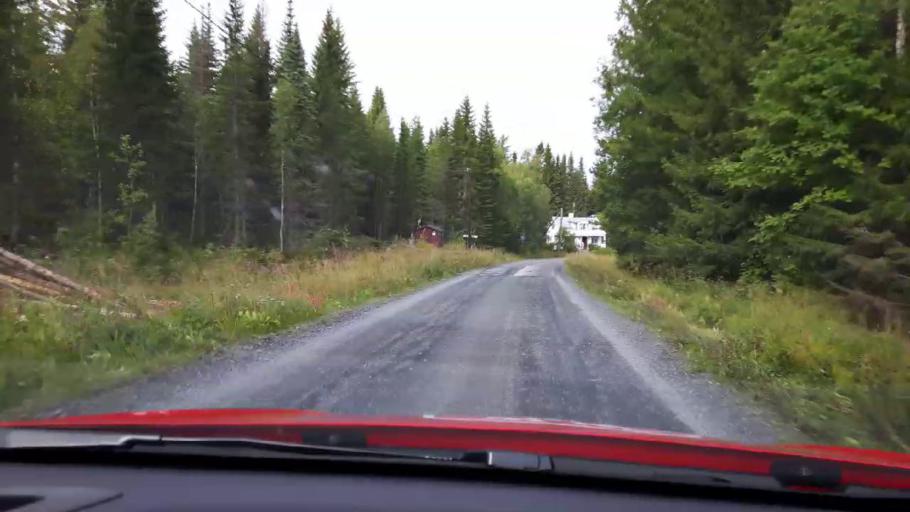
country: SE
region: Jaemtland
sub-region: Are Kommun
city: Jarpen
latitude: 63.2810
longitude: 13.7304
